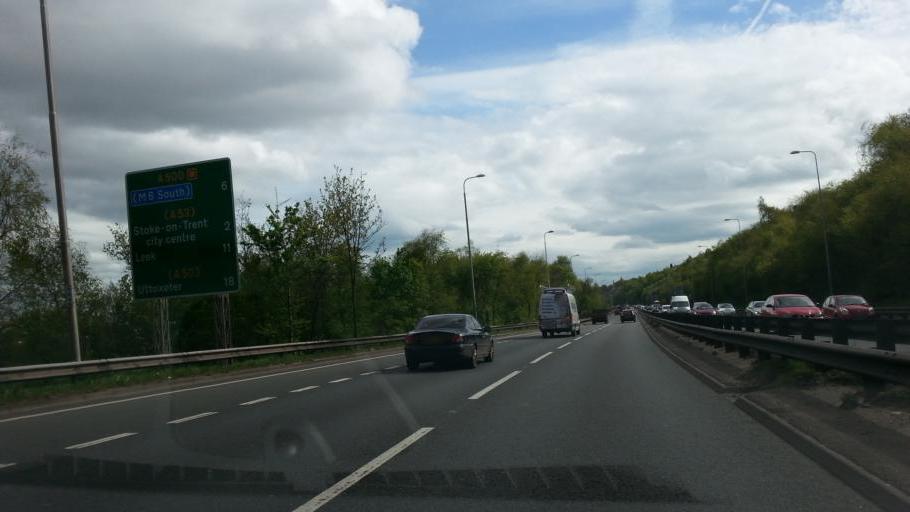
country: GB
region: England
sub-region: Stoke-on-Trent
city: Stoke-on-Trent
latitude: 53.0299
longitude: -2.2075
